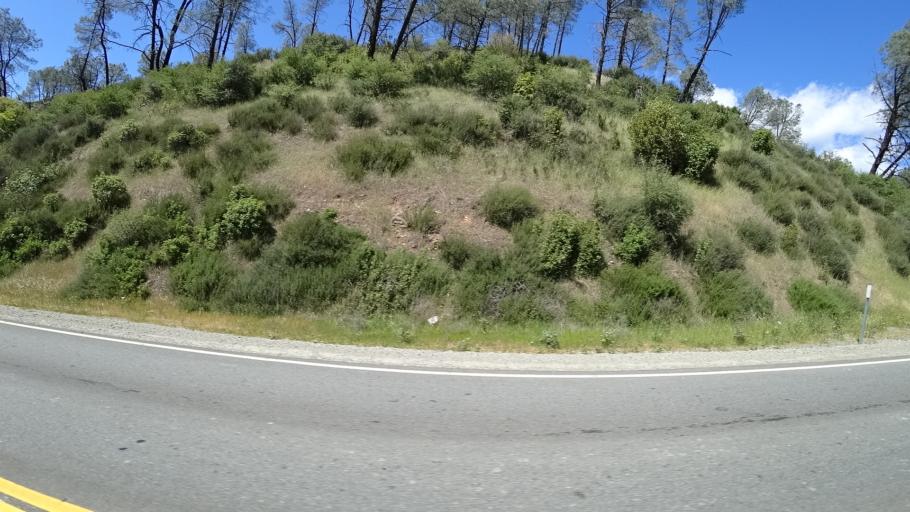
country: US
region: California
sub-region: Trinity County
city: Weaverville
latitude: 40.7323
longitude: -123.0232
